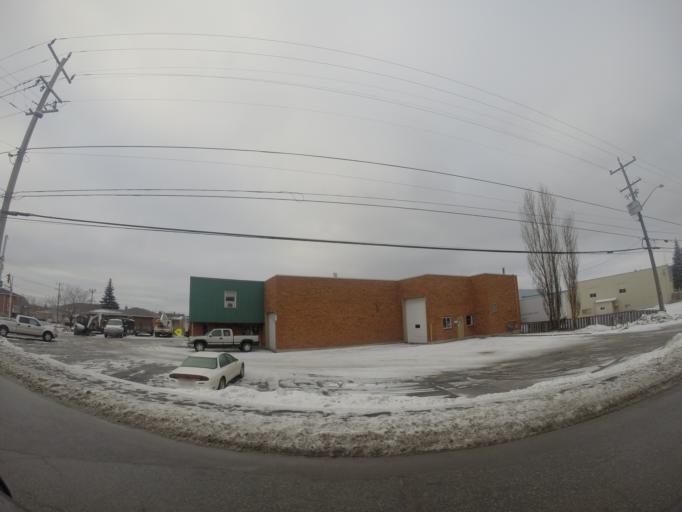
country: CA
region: Ontario
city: Greater Sudbury
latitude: 46.4647
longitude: -81.0288
